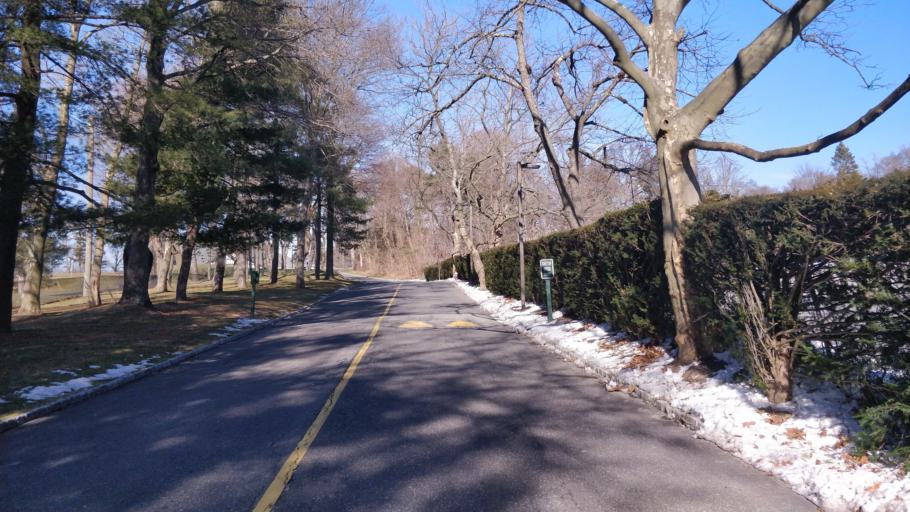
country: US
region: New York
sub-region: Nassau County
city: Old Westbury
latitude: 40.8004
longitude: -73.5984
